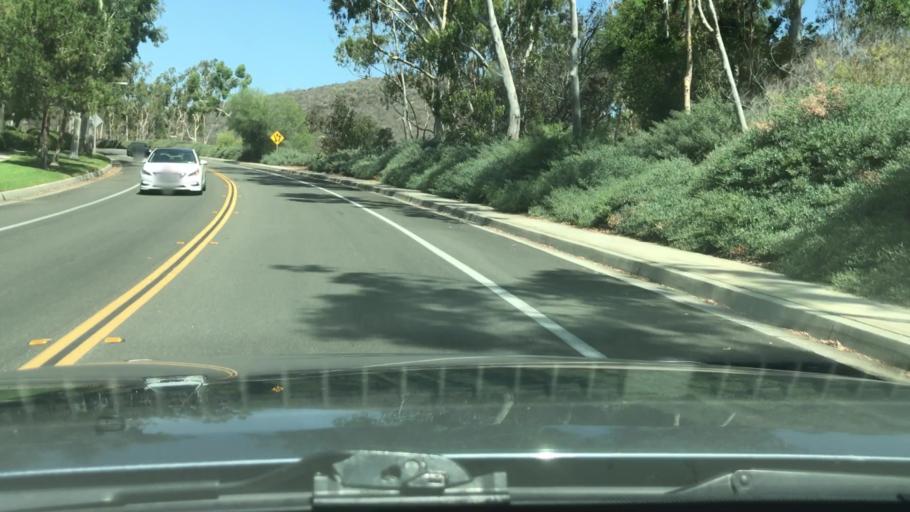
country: US
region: California
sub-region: Orange County
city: Irvine
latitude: 33.6393
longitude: -117.8011
